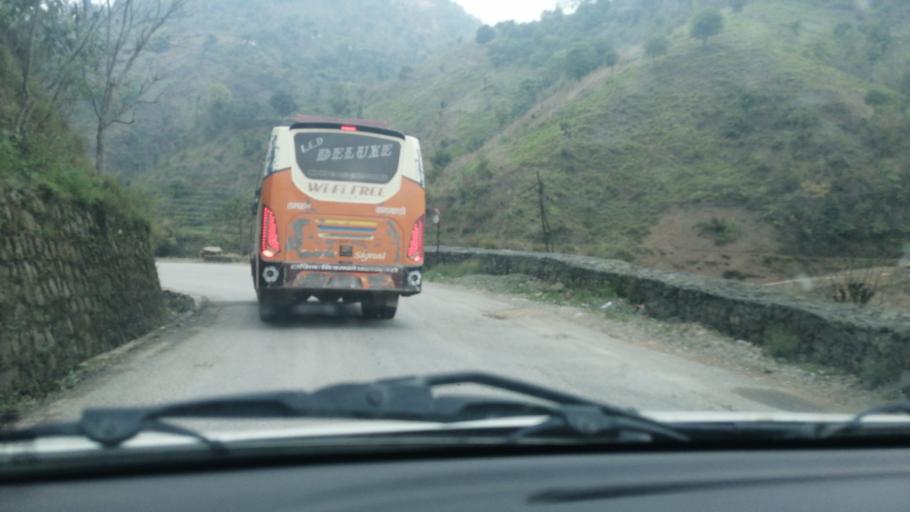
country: NP
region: Western Region
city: Tansen
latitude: 27.8089
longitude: 83.5169
